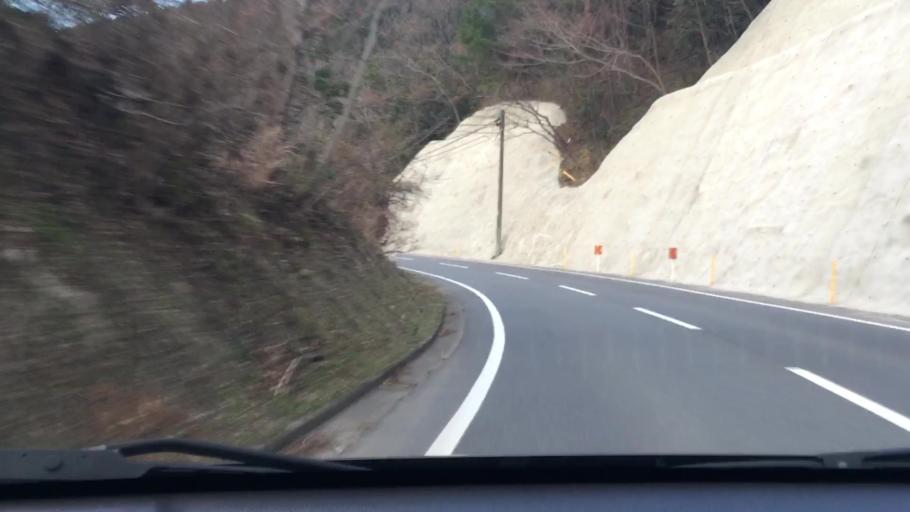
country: JP
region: Oita
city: Hiji
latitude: 33.3691
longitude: 131.4662
